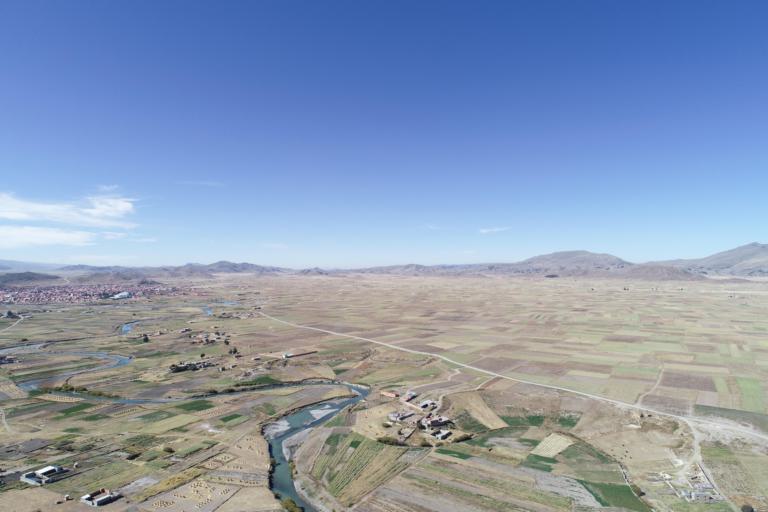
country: BO
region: La Paz
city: Achacachi
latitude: -16.0265
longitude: -68.7125
